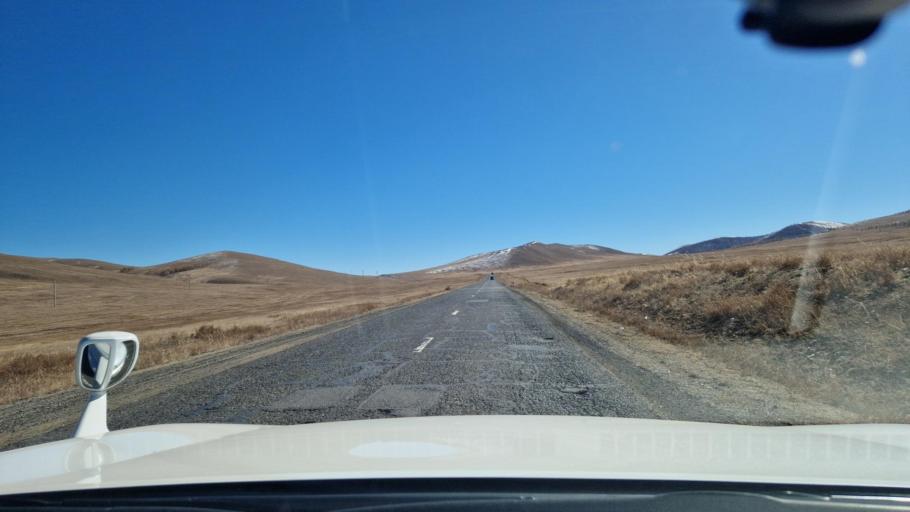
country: MN
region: Hentiy
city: Modot
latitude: 47.7878
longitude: 108.8311
